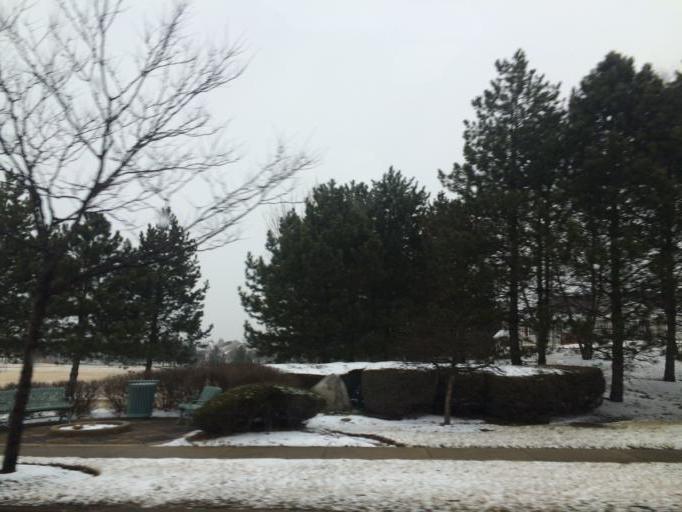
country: US
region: Illinois
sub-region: Cook County
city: Streamwood
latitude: 42.0277
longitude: -88.1510
